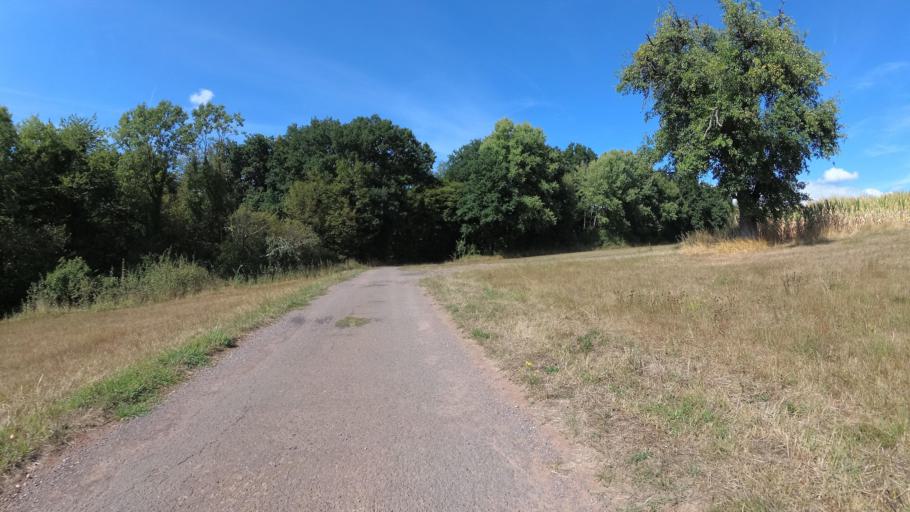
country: DE
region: Saarland
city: Mainzweiler
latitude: 49.4082
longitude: 7.0843
